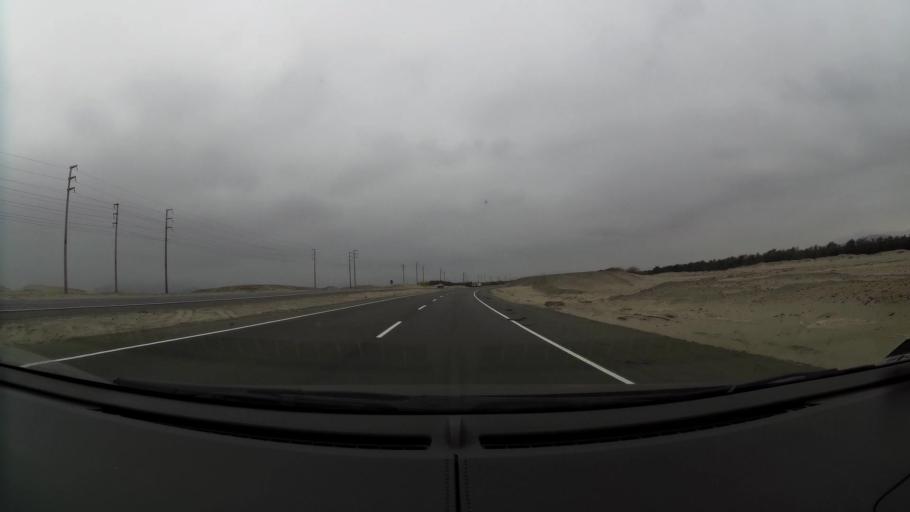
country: PE
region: La Libertad
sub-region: Viru
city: Chao
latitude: -8.6062
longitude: -78.6668
